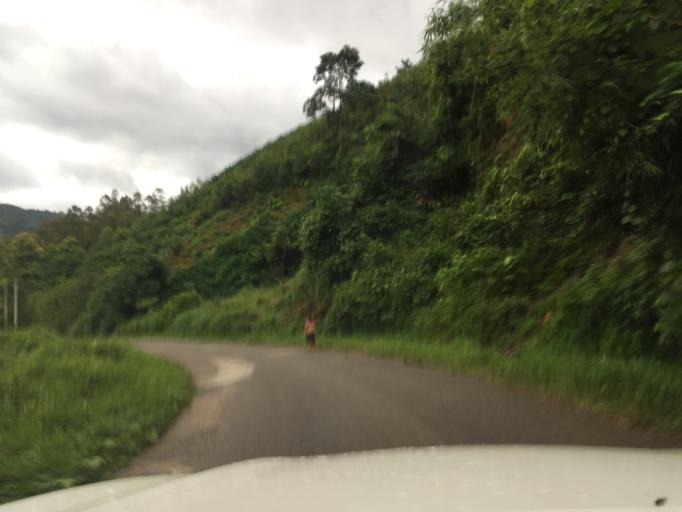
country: LA
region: Oudomxai
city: Muang La
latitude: 20.9782
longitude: 102.2233
